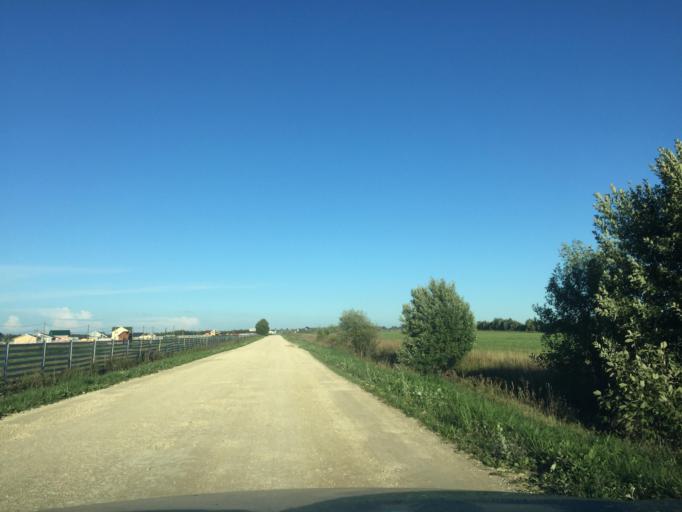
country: RU
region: Leningrad
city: Rozhdestveno
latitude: 59.3327
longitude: 30.0021
